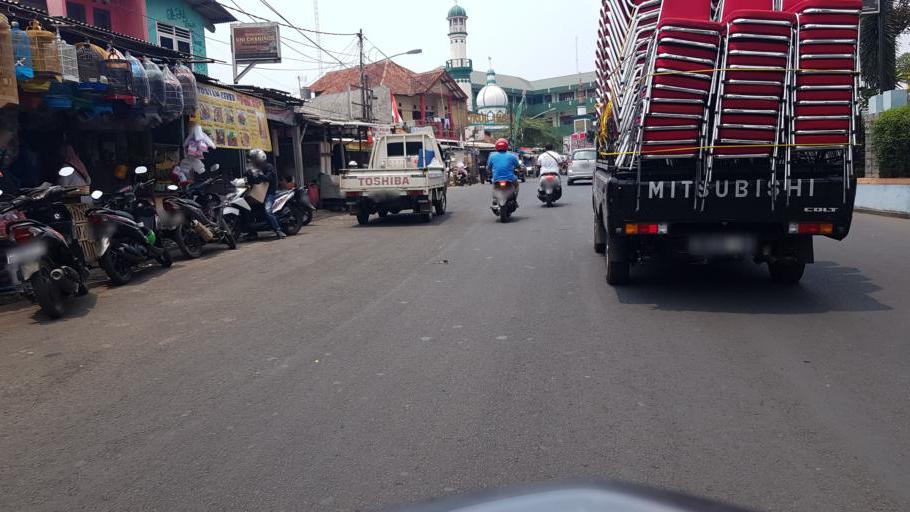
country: ID
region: West Java
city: Bekasi
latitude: -6.2829
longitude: 106.9110
